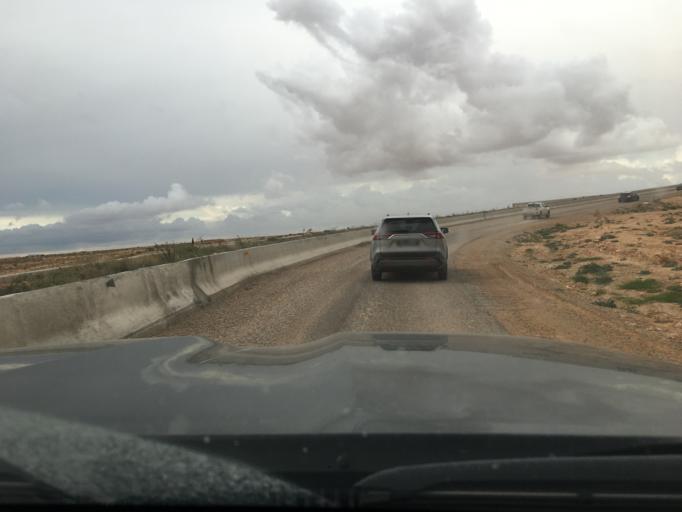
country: TN
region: Madanin
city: Medenine
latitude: 33.2973
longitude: 10.6088
